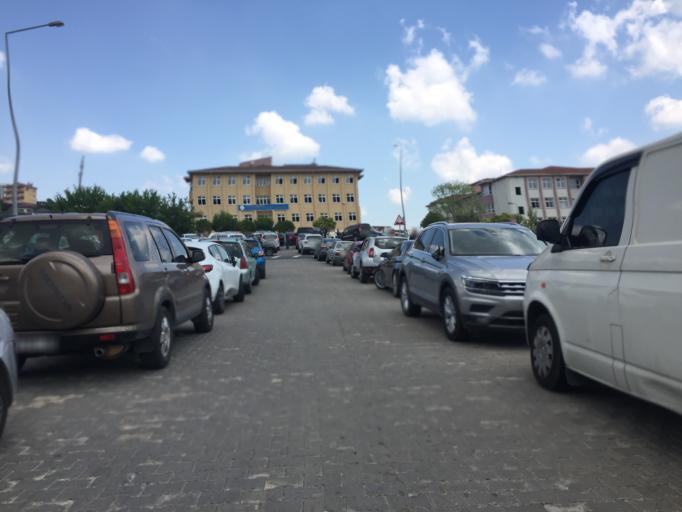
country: TR
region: Istanbul
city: Esenyurt
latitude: 41.0795
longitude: 28.6624
